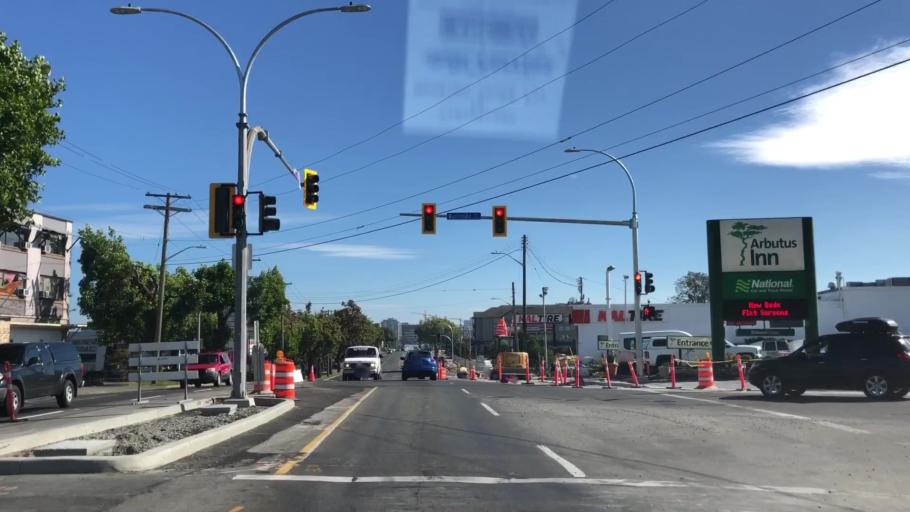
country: CA
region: British Columbia
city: Victoria
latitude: 48.4421
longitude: -123.3691
